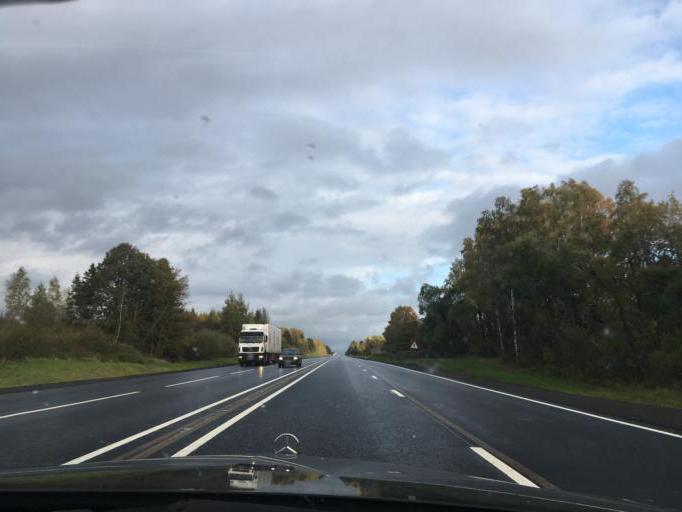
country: RU
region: Smolensk
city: Katyn'
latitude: 54.8450
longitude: 31.6954
